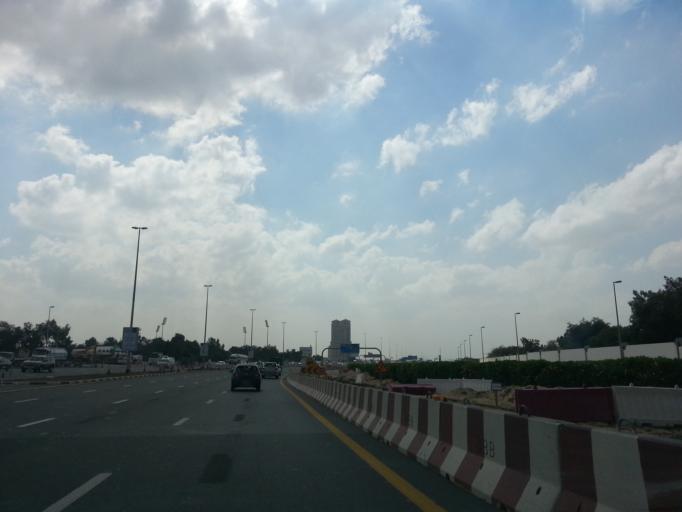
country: AE
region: Ash Shariqah
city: Sharjah
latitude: 25.2255
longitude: 55.3153
